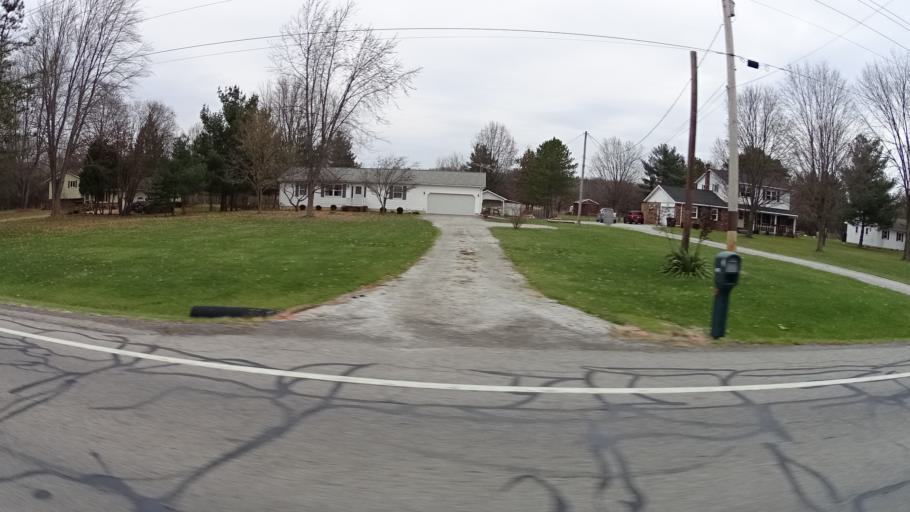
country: US
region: Ohio
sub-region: Lorain County
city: Lagrange
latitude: 41.1684
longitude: -82.0997
